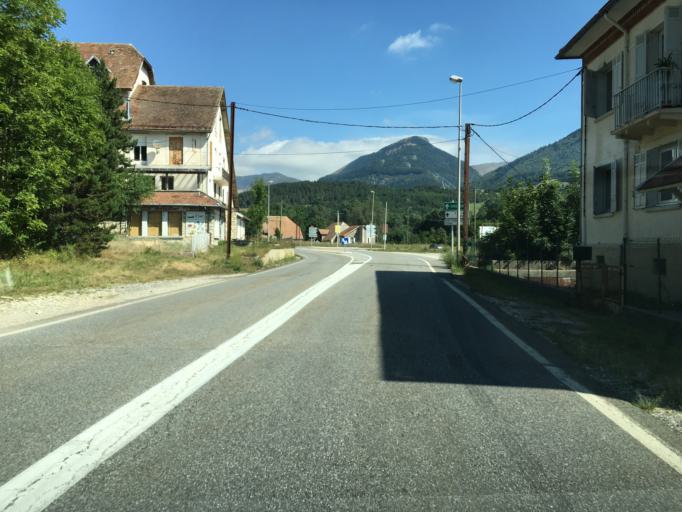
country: FR
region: Rhone-Alpes
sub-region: Departement de l'Isere
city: Mens
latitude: 44.6707
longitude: 5.6979
